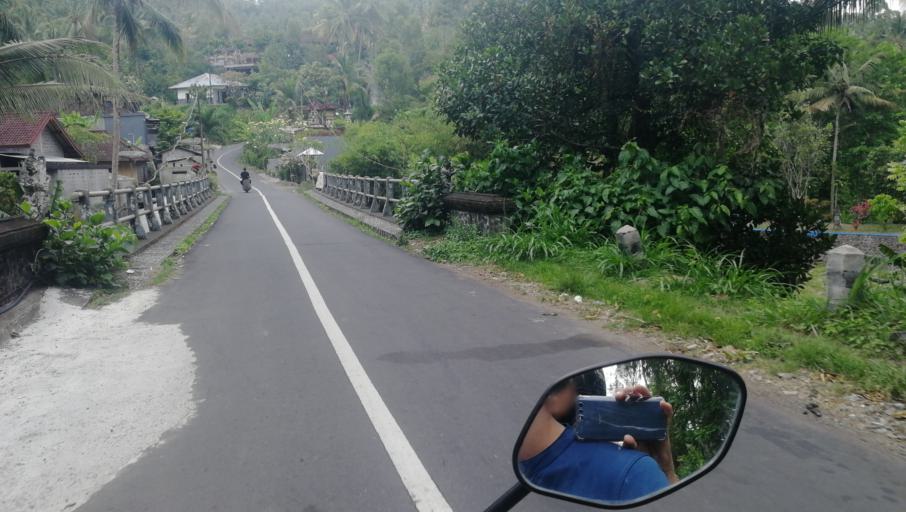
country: ID
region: Bali
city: Banjar Tamansari
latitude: -8.2674
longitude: 115.0204
